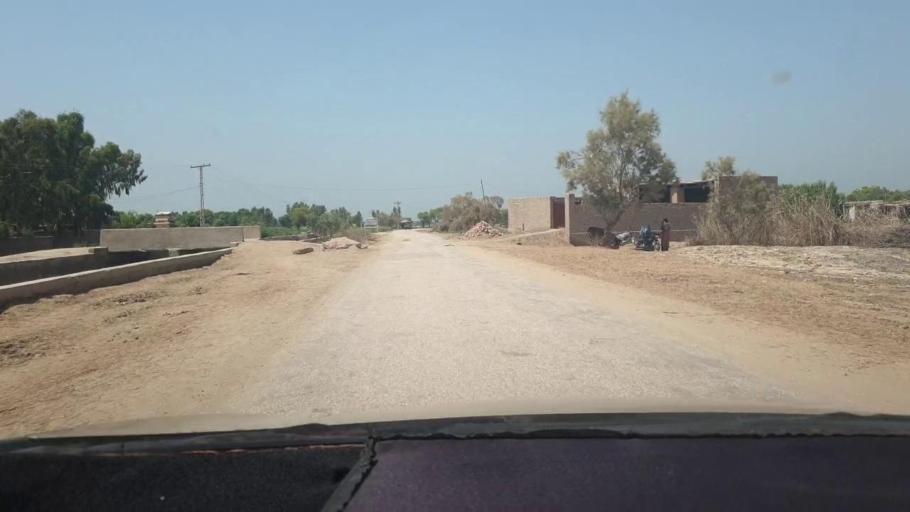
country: PK
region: Sindh
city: Miro Khan
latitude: 27.6694
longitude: 68.0619
